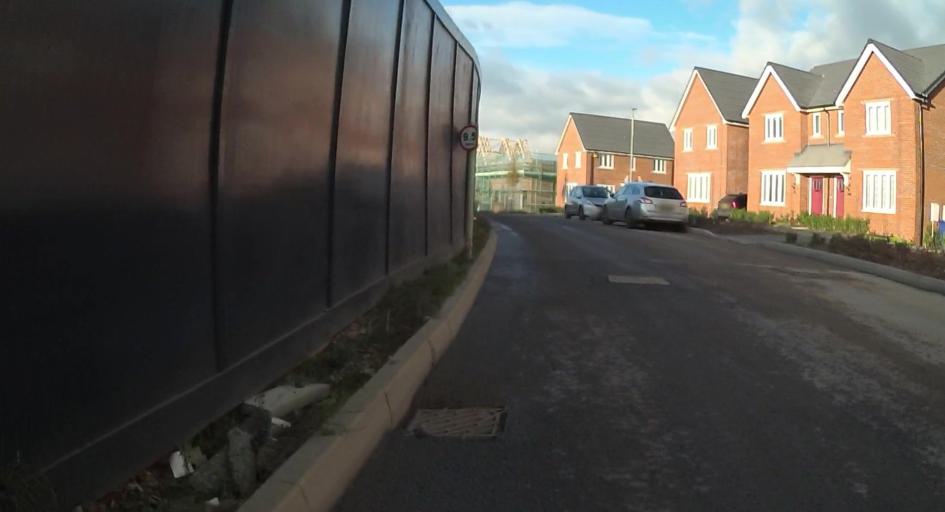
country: GB
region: England
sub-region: Bracknell Forest
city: Binfield
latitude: 51.4269
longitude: -0.7776
